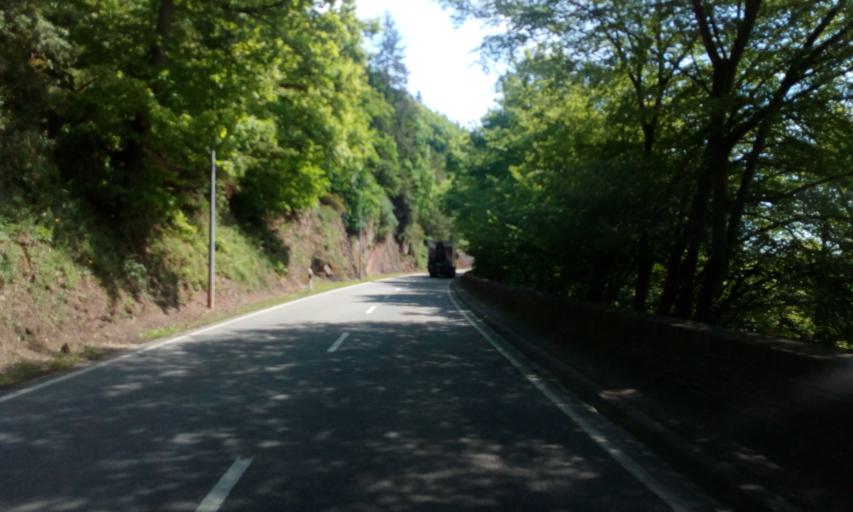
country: LU
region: Diekirch
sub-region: Canton de Vianden
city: Vianden
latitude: 49.9306
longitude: 6.2238
